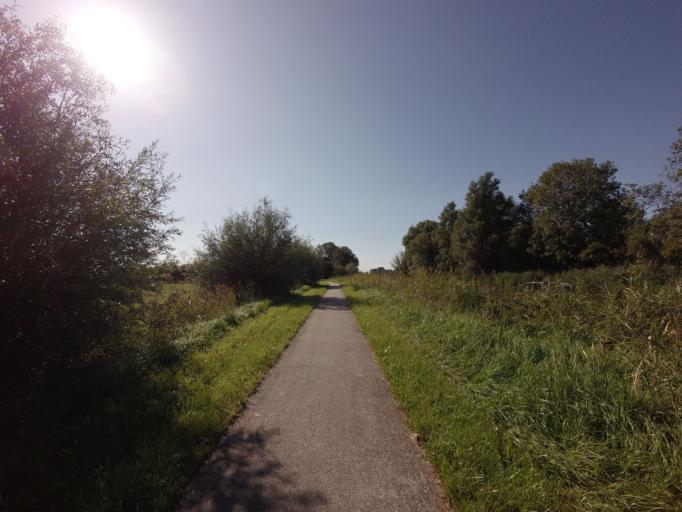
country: NL
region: Friesland
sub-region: Gemeente Leeuwarden
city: Wirdum
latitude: 53.1577
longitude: 5.7656
